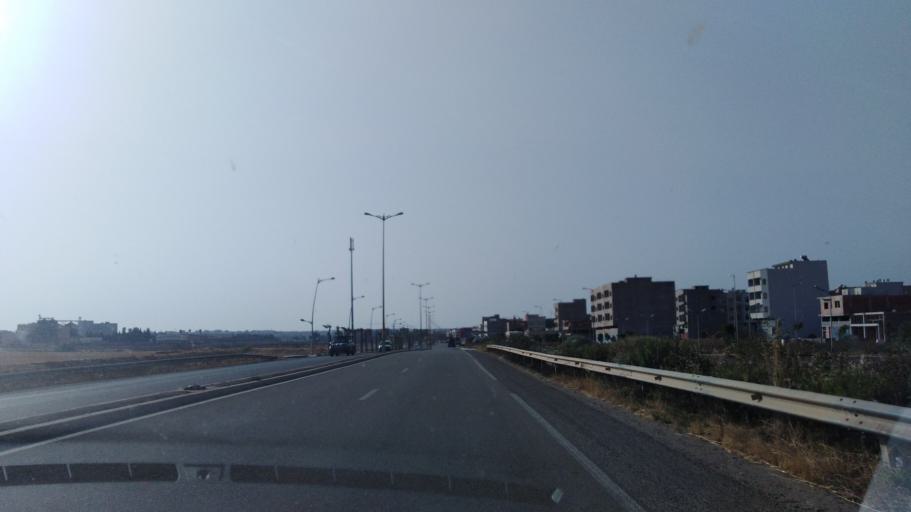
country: MA
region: Chaouia-Ouardigha
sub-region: Settat Province
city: Settat
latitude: 32.9796
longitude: -7.6060
